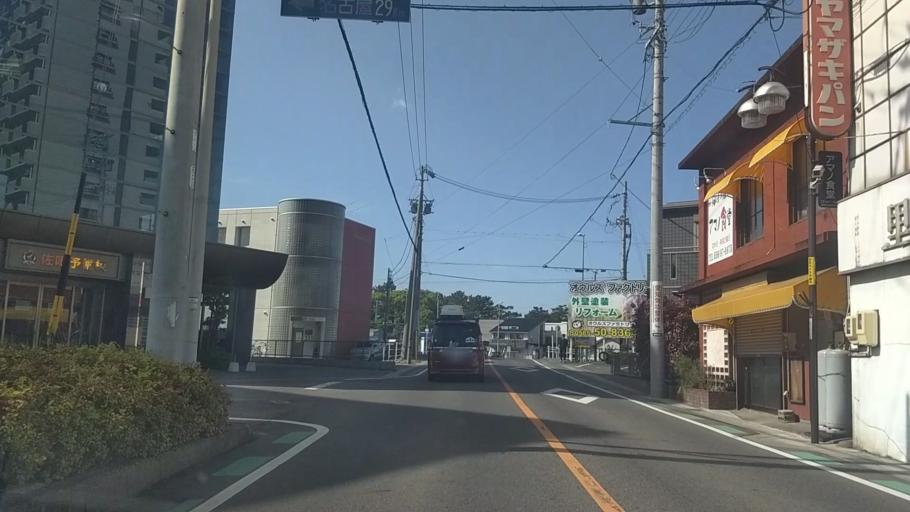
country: JP
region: Aichi
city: Anjo
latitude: 34.9886
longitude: 137.0838
